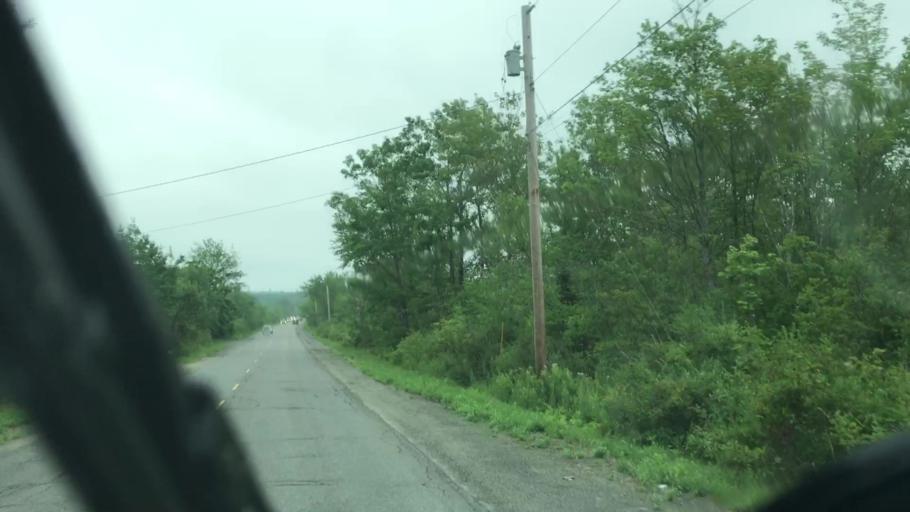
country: US
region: Maine
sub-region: Penobscot County
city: Veazie
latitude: 44.8746
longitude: -68.7138
